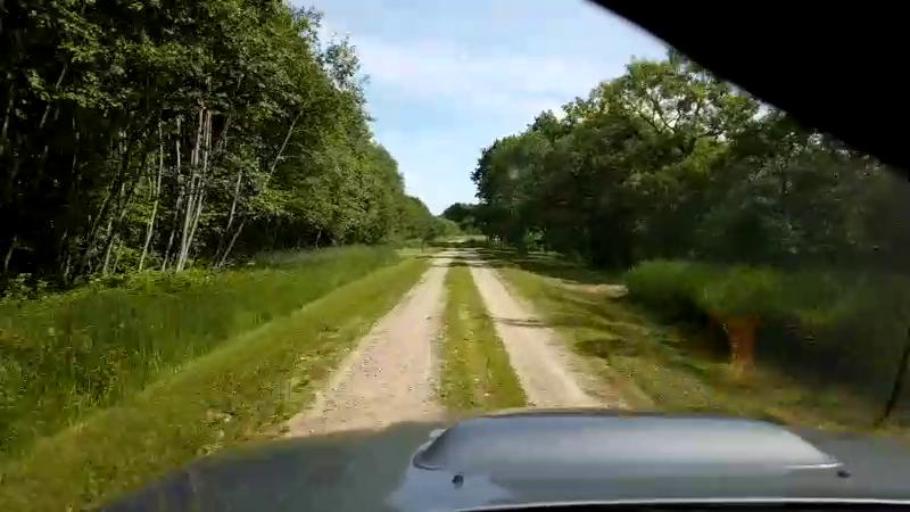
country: EE
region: Paernumaa
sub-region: Sauga vald
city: Sauga
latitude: 58.4973
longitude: 24.5407
